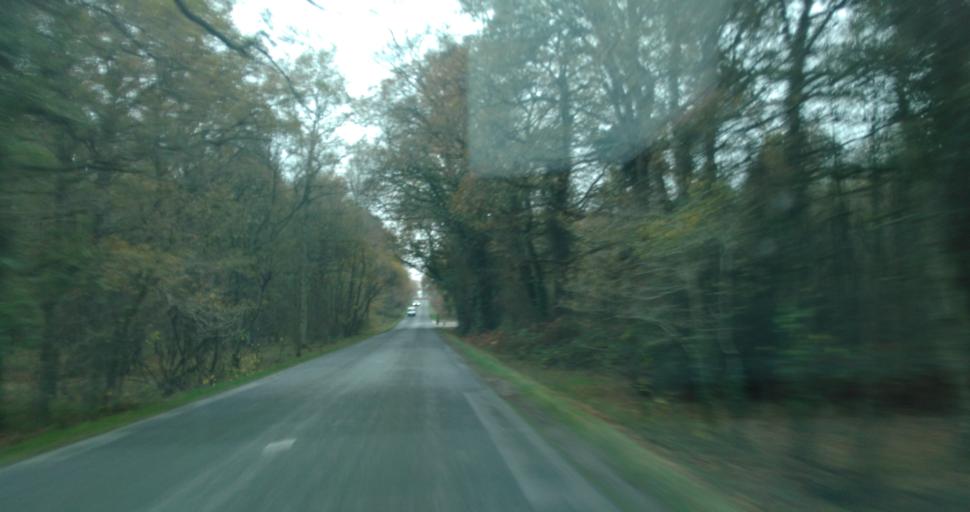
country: FR
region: Brittany
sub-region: Departement d'Ille-et-Vilaine
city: Iffendic
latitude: 48.0971
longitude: -2.0441
